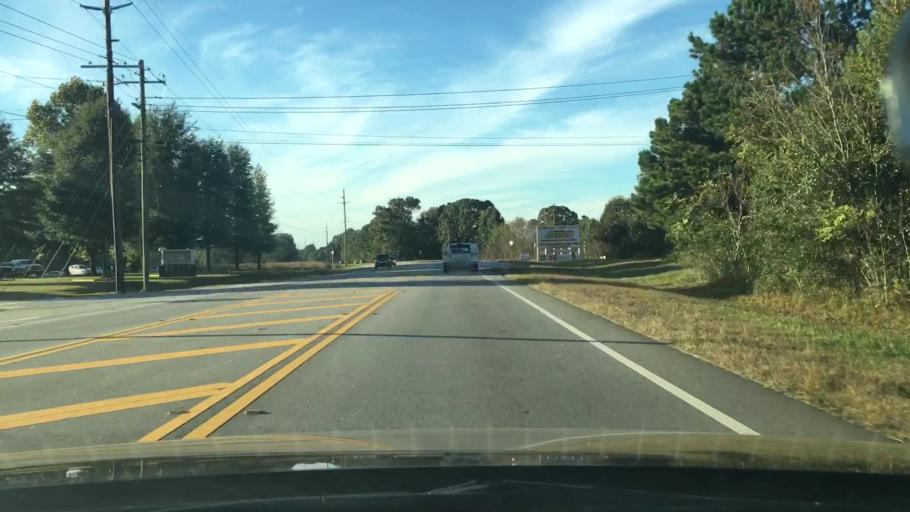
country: US
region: Georgia
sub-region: Coweta County
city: Senoia
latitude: 33.3044
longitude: -84.5972
